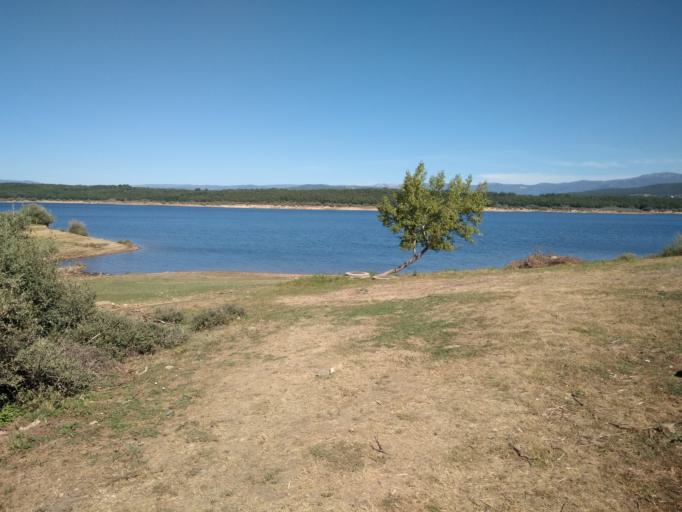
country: ES
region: Castille and Leon
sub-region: Provincia de Zamora
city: Manzanal de Arriba
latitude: 42.0077
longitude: -6.4804
